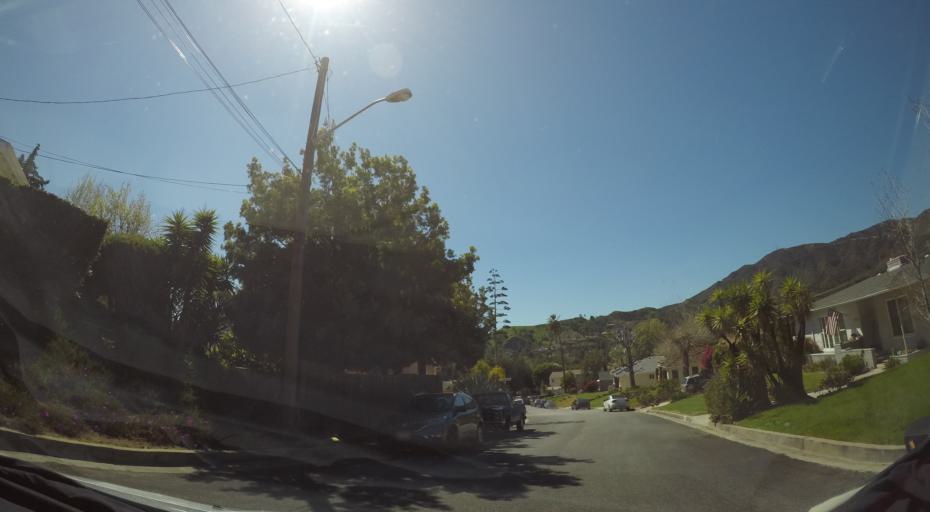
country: US
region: California
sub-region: Los Angeles County
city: La Canada Flintridge
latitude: 34.1765
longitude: -118.2238
